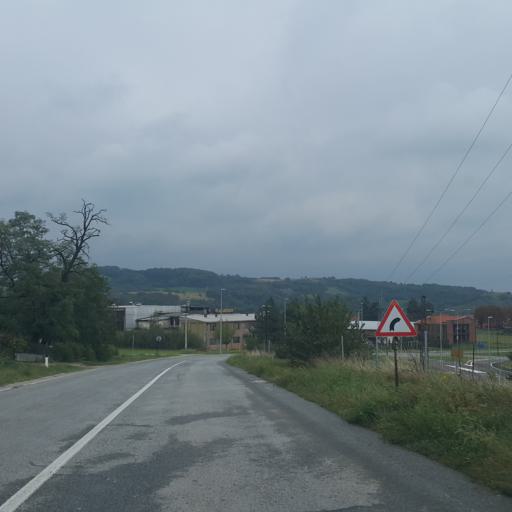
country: RS
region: Central Serbia
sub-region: Nisavski Okrug
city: Razanj
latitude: 43.6849
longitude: 21.5460
